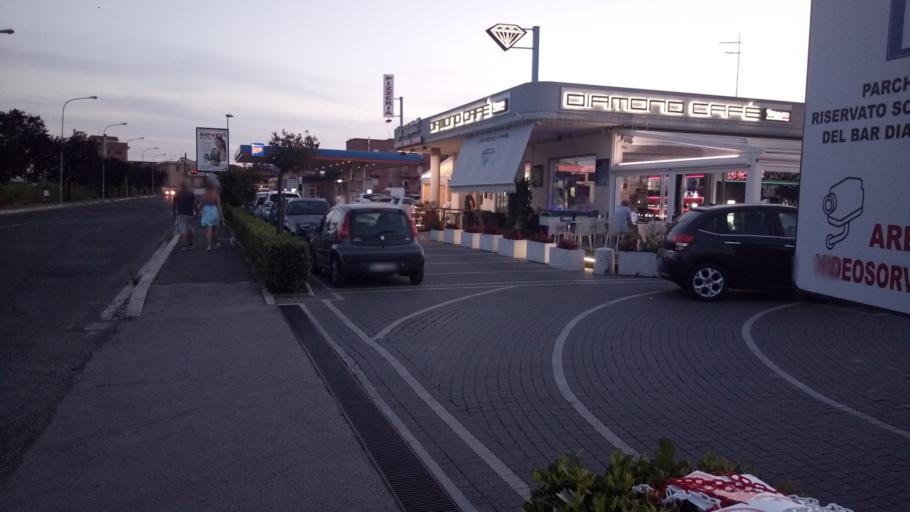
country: IT
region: Latium
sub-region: Citta metropolitana di Roma Capitale
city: Ciampino
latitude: 41.8092
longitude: 12.5997
